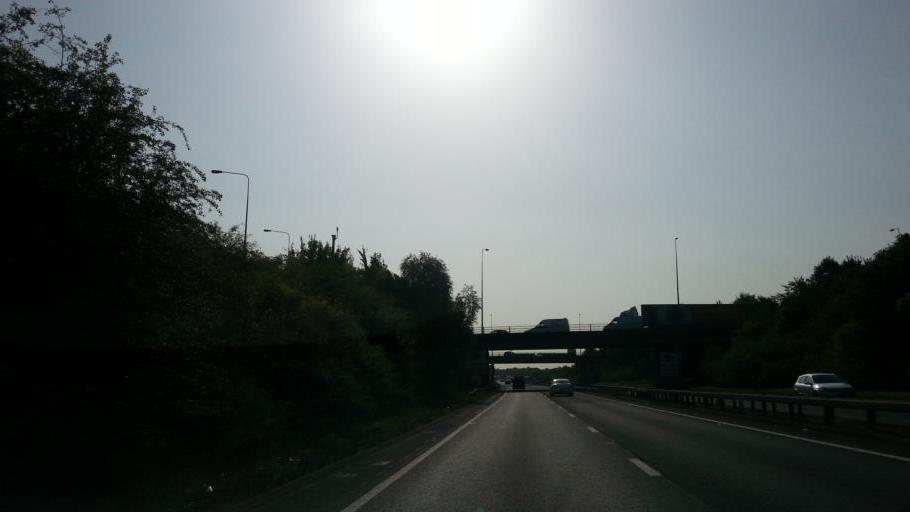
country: GB
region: England
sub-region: Cambridgeshire
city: Great Stukeley
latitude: 52.3415
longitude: -0.2103
